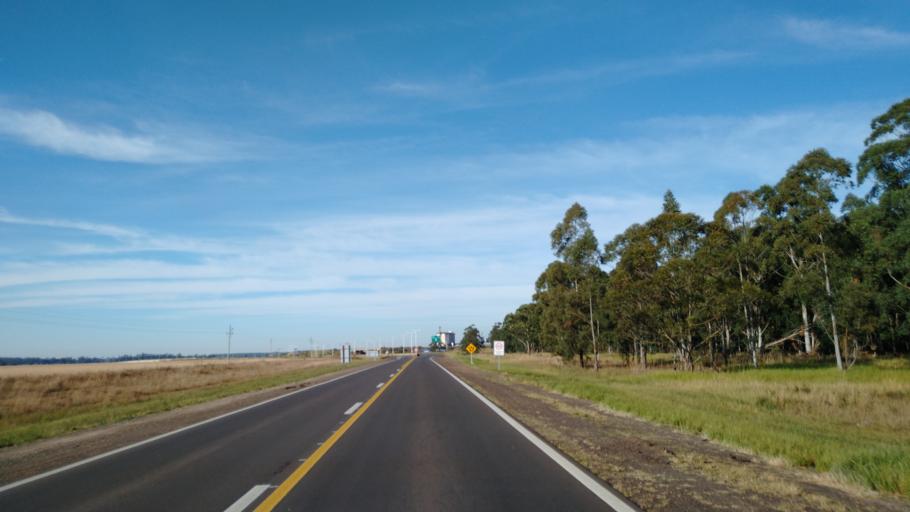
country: AR
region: Corrientes
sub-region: Departamento de Paso de los Libres
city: Paso de los Libres
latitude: -29.7038
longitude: -57.2109
